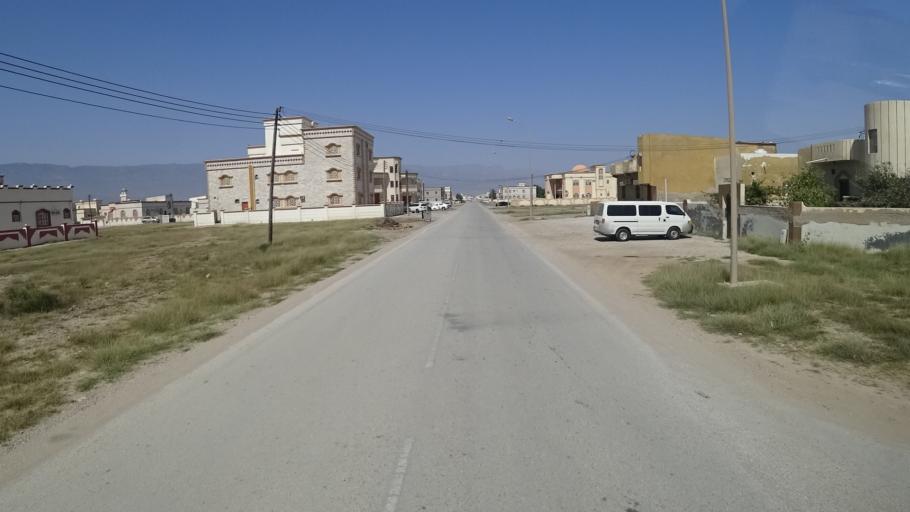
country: OM
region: Zufar
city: Salalah
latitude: 16.9825
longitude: 54.7063
